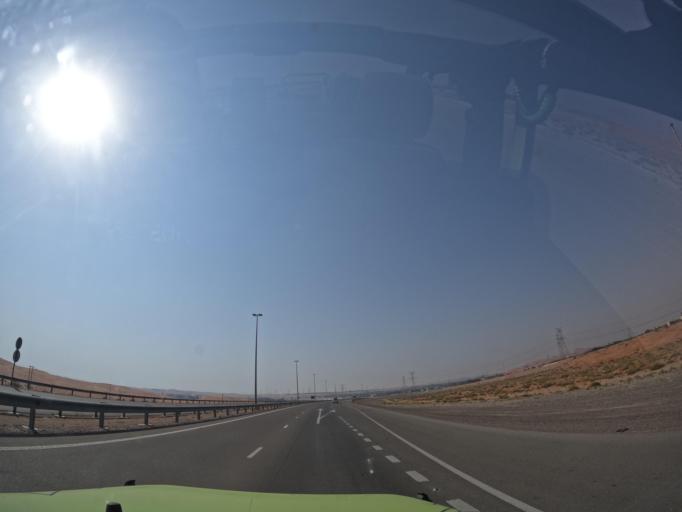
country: OM
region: Al Buraimi
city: Al Buraymi
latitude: 24.3751
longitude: 55.7284
